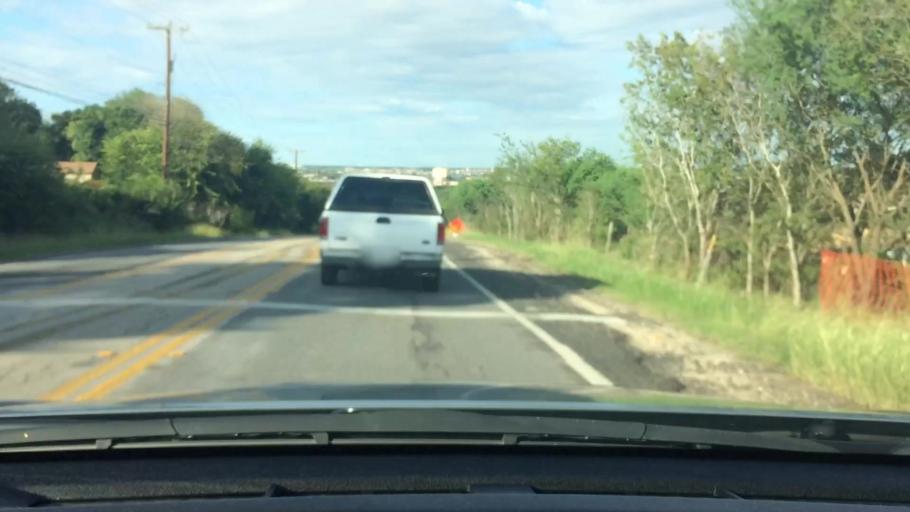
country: US
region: Texas
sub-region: Bexar County
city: Converse
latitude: 29.4943
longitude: -98.3110
